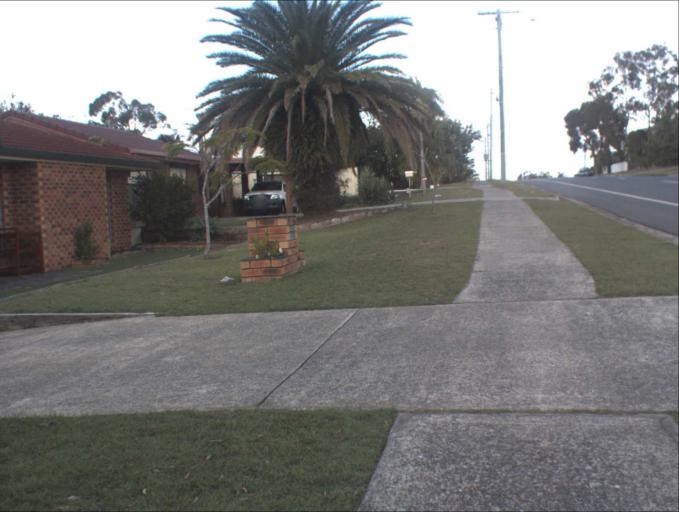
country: AU
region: Queensland
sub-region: Brisbane
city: Sunnybank Hills
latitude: -27.6654
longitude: 153.0390
